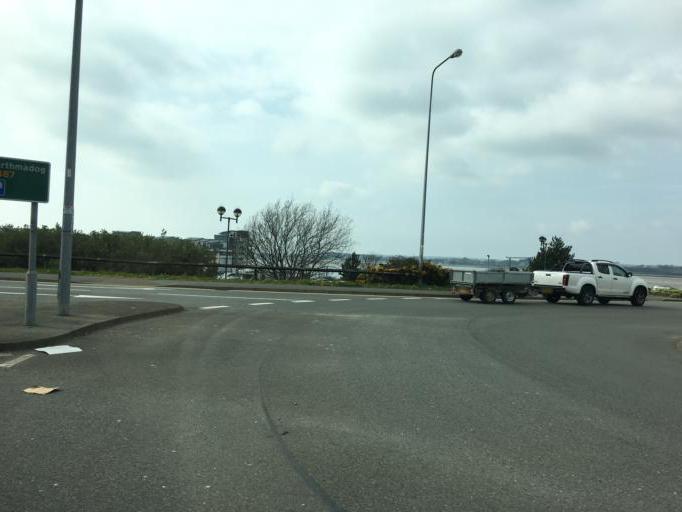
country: GB
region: Wales
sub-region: Gwynedd
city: Caernarfon
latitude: 53.1455
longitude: -4.2703
